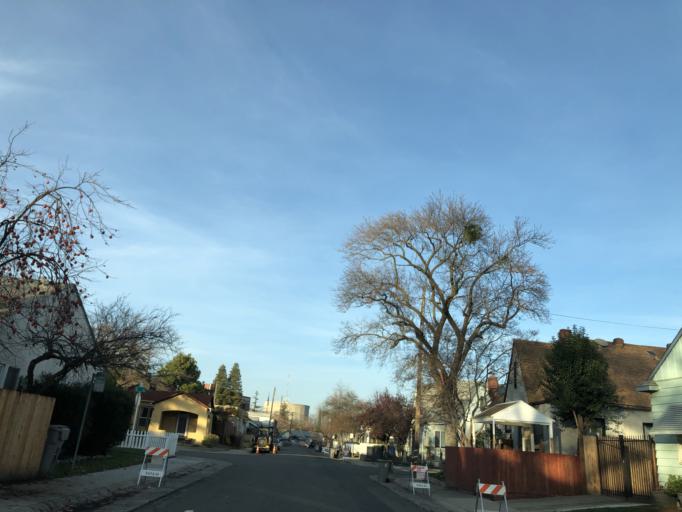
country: US
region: California
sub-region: Sacramento County
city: Sacramento
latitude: 38.5664
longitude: -121.4657
